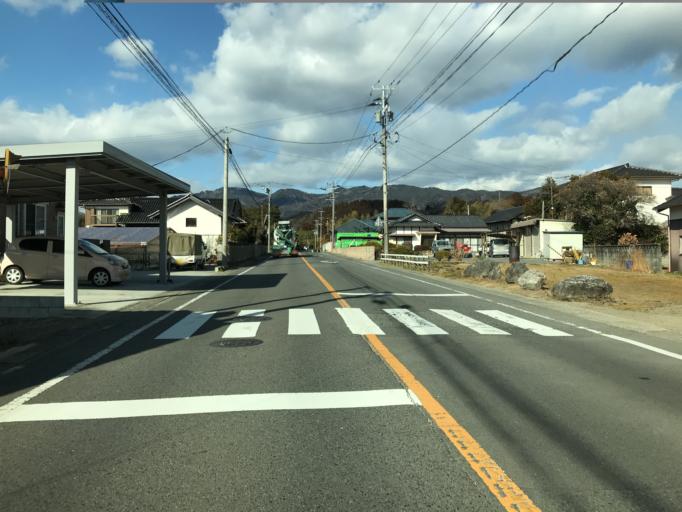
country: JP
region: Fukushima
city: Iwaki
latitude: 37.1178
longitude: 140.8710
